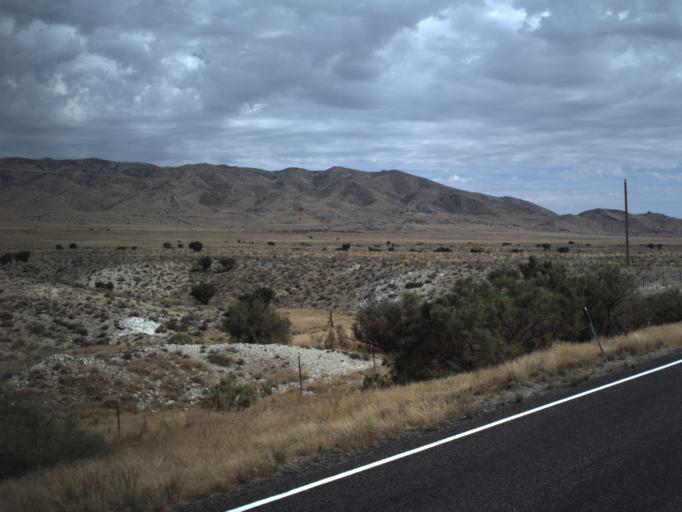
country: US
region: Utah
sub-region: Tooele County
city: Wendover
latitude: 41.4376
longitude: -113.7362
